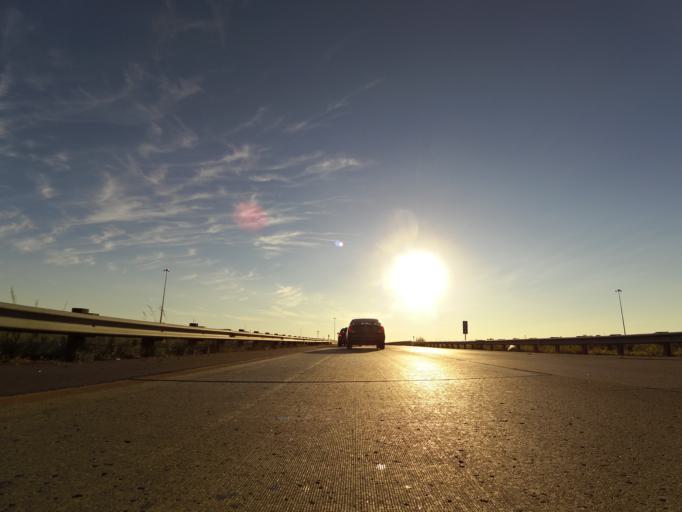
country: US
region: Kansas
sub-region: Sedgwick County
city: Park City
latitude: 37.7559
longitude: -97.3714
